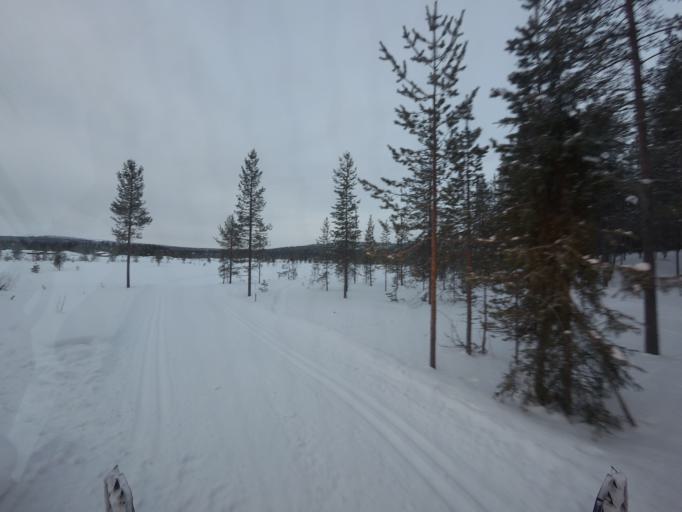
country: FI
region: Lapland
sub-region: Tunturi-Lappi
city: Kolari
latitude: 67.6201
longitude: 24.1332
